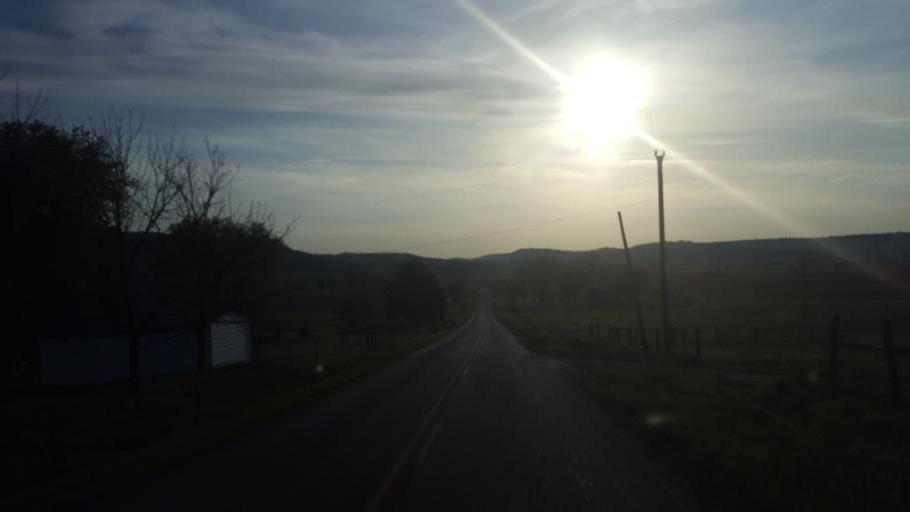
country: US
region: Kentucky
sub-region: Hart County
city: Horse Cave
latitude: 37.2203
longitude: -85.9568
